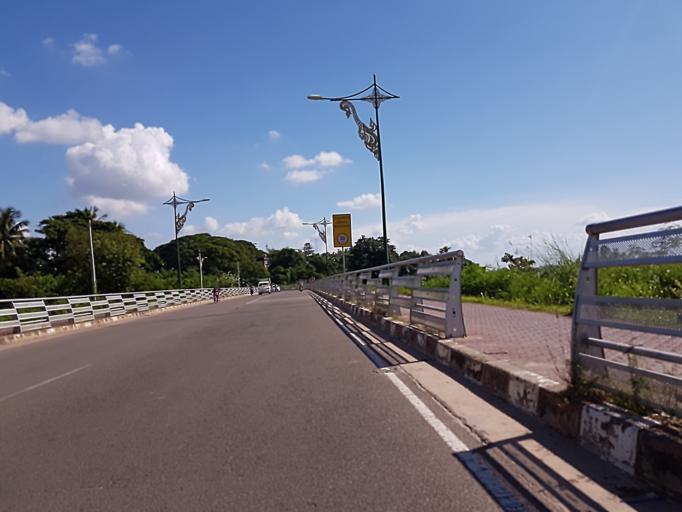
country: LA
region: Vientiane
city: Vientiane
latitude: 17.9409
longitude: 102.6172
